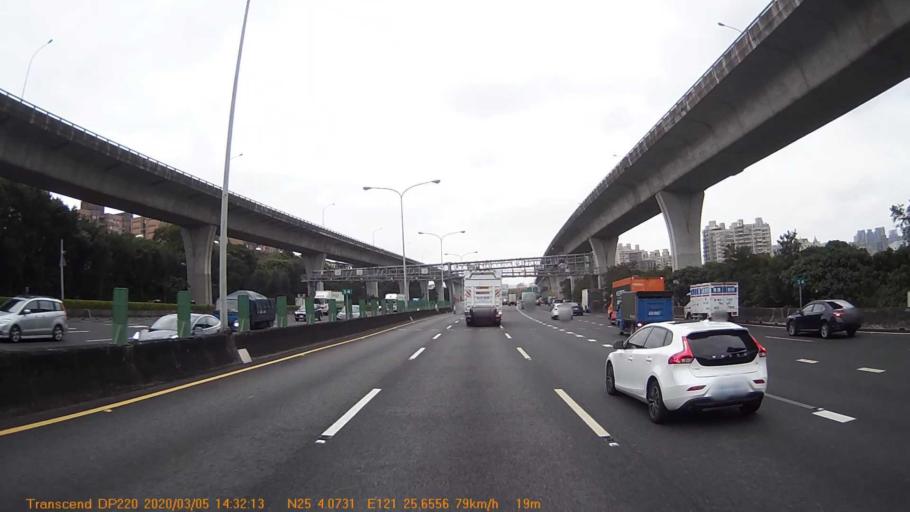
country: TW
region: Taipei
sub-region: Taipei
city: Banqiao
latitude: 25.0658
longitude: 121.4297
